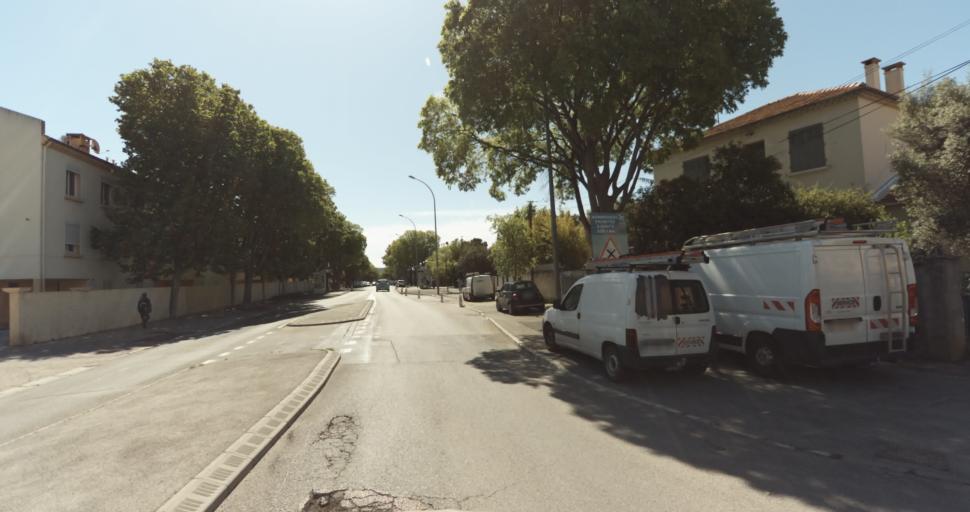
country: FR
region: Provence-Alpes-Cote d'Azur
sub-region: Departement du Var
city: Six-Fours-les-Plages
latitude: 43.1073
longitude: 5.8644
